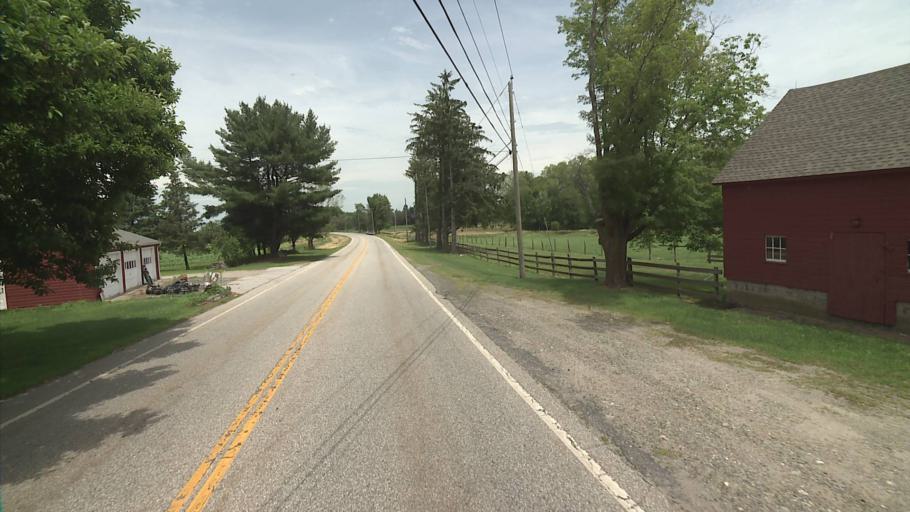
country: US
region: Connecticut
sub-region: New London County
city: Preston City
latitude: 41.5399
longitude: -71.9683
